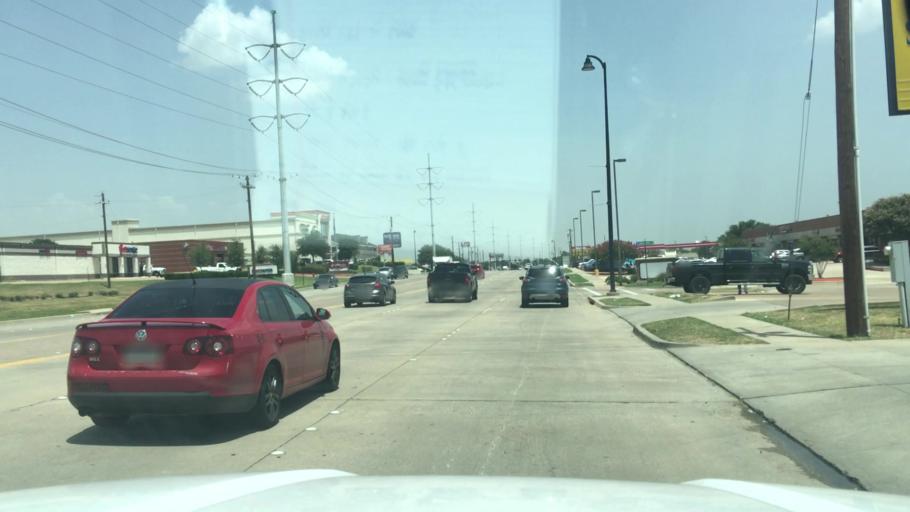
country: US
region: Texas
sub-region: Tarrant County
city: North Richland Hills
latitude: 32.8473
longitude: -97.2385
